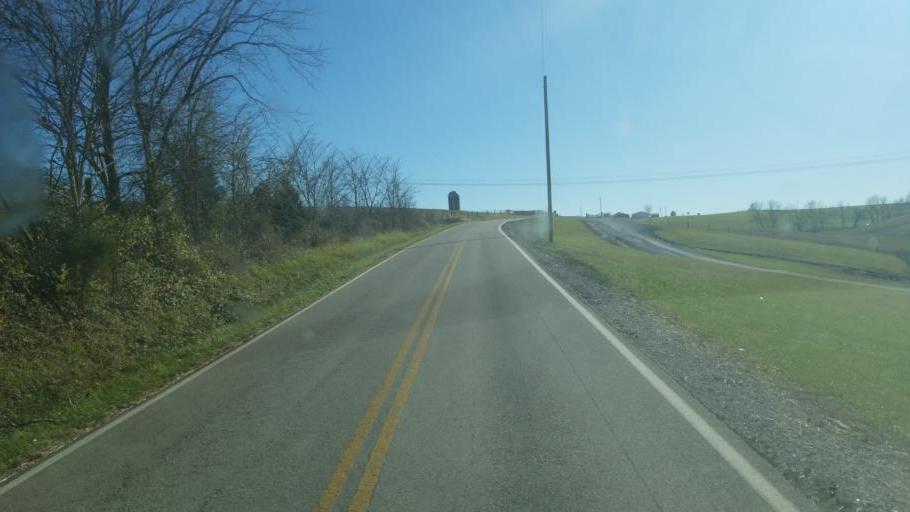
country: US
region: Kentucky
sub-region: Mason County
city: Maysville
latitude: 38.5498
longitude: -83.6403
